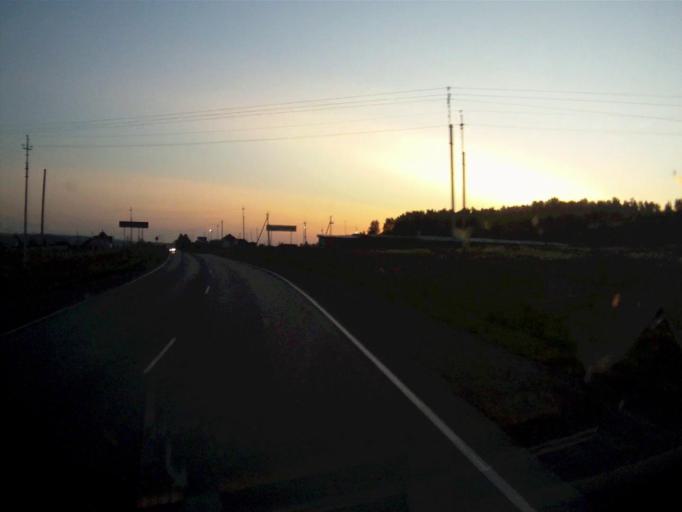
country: RU
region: Chelyabinsk
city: Poletayevo
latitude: 55.2250
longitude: 60.9954
